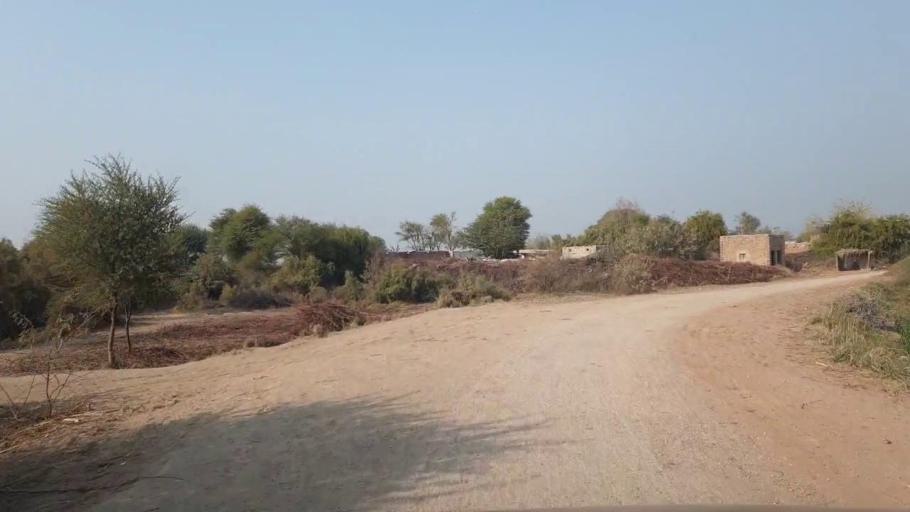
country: PK
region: Sindh
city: Bhit Shah
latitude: 25.8973
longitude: 68.4713
